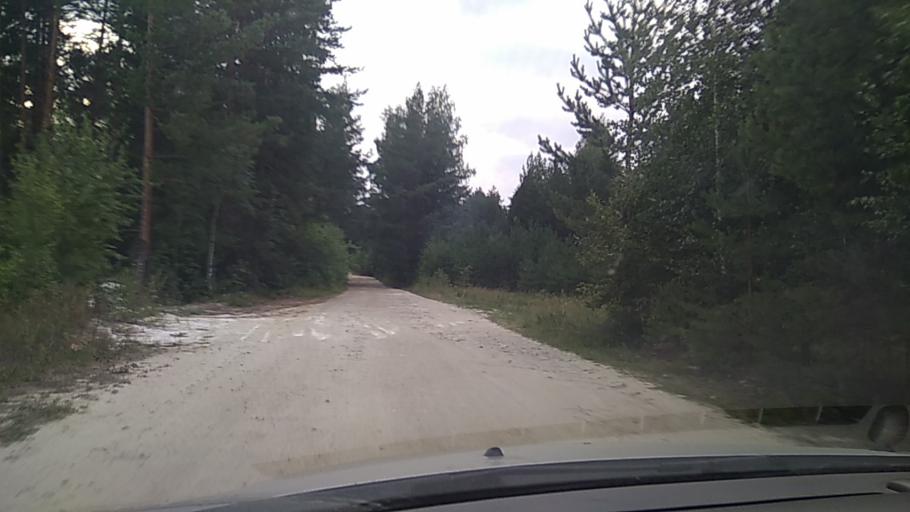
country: RU
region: Chelyabinsk
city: Kyshtym
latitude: 55.6798
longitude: 60.5781
